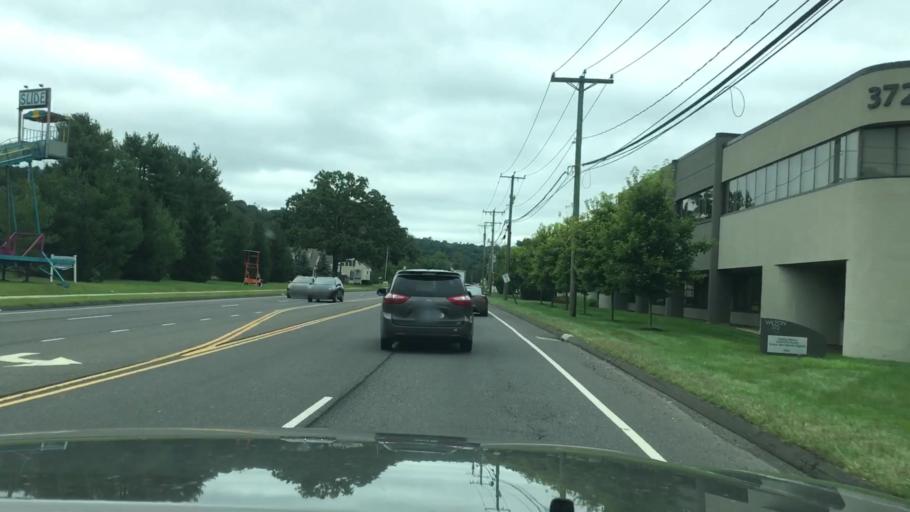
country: US
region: Connecticut
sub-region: Fairfield County
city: Wilton
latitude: 41.2065
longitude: -73.4304
